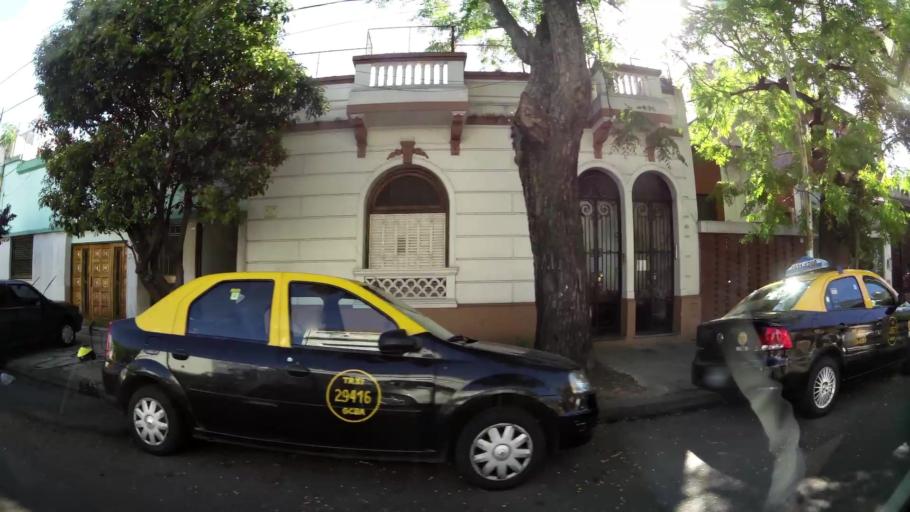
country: AR
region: Buenos Aires F.D.
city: Villa Santa Rita
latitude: -34.6127
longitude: -58.4668
